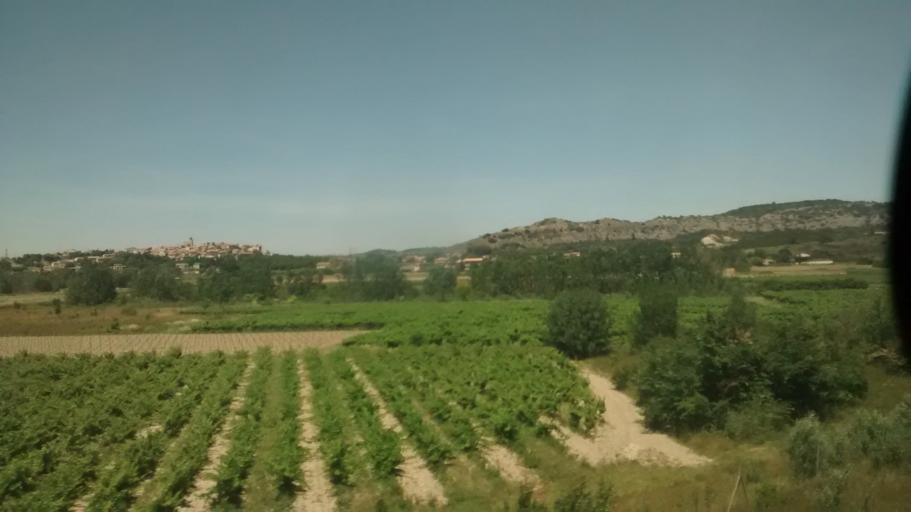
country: FR
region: Languedoc-Roussillon
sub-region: Departement du Gard
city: Montfrin
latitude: 43.8883
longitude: 4.6284
